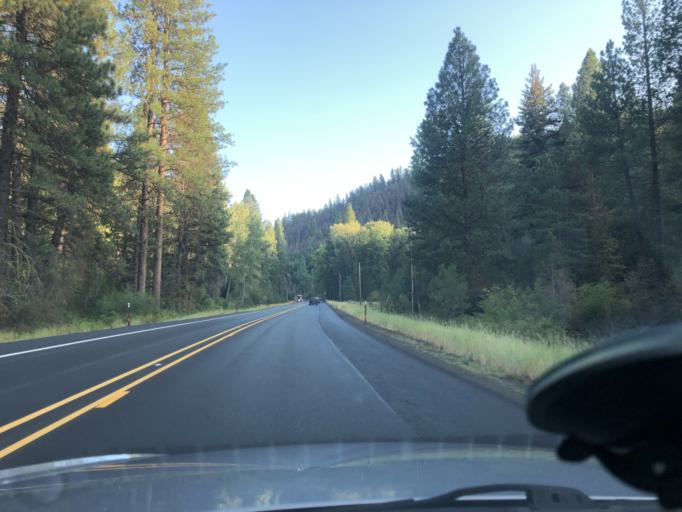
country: US
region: Washington
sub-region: Kittitas County
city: Cle Elum
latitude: 47.2600
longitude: -120.6956
